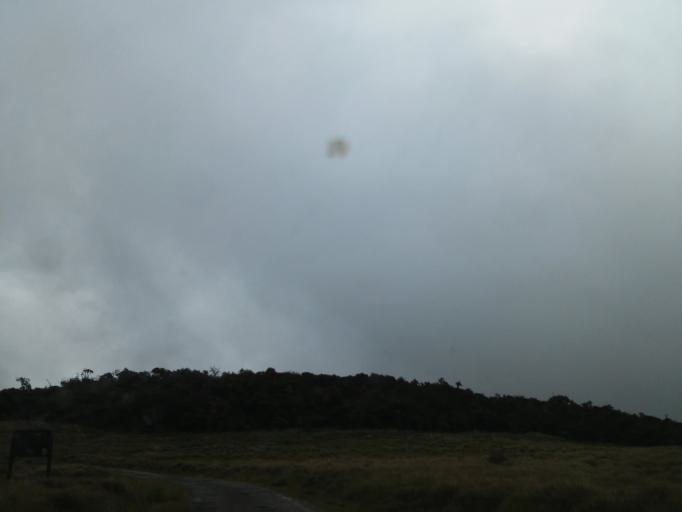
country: LK
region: Uva
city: Haputale
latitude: 6.7941
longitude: 80.8200
